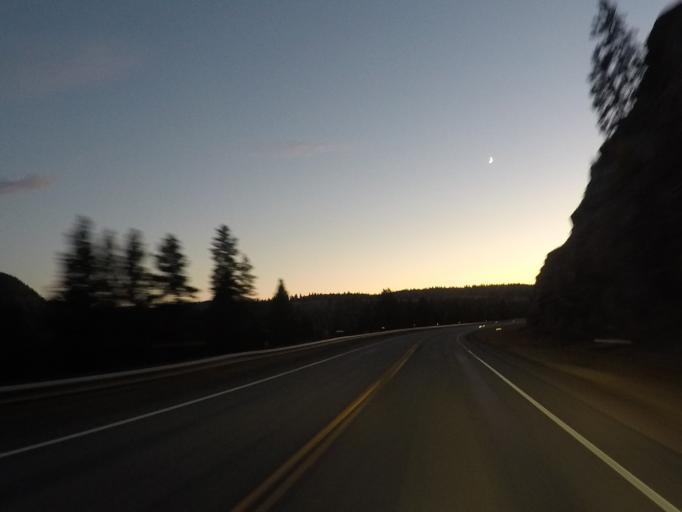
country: US
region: Montana
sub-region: Missoula County
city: Seeley Lake
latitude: 47.0144
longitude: -113.3224
